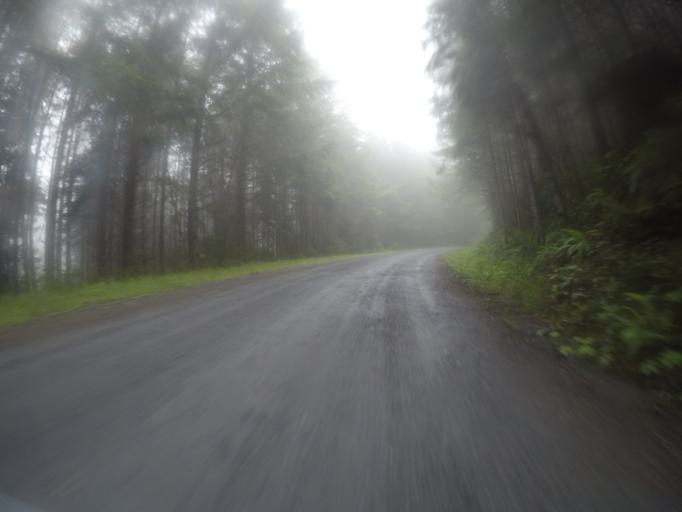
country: US
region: California
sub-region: Humboldt County
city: Westhaven-Moonstone
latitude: 41.2404
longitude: -123.9891
